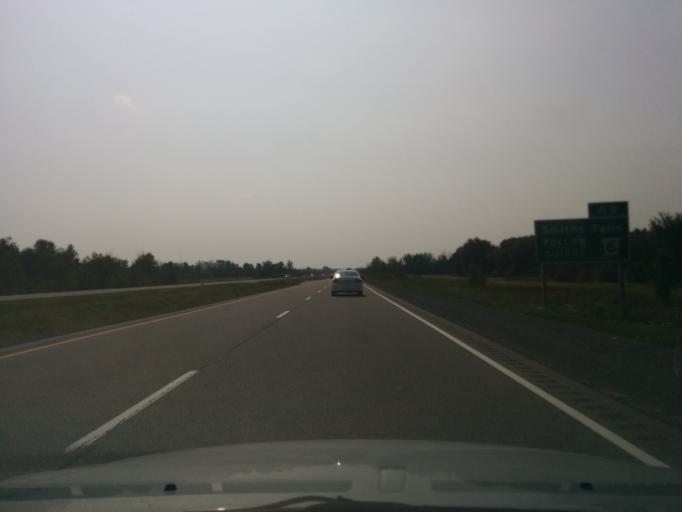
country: CA
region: Ontario
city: Bells Corners
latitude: 45.1555
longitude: -75.6847
